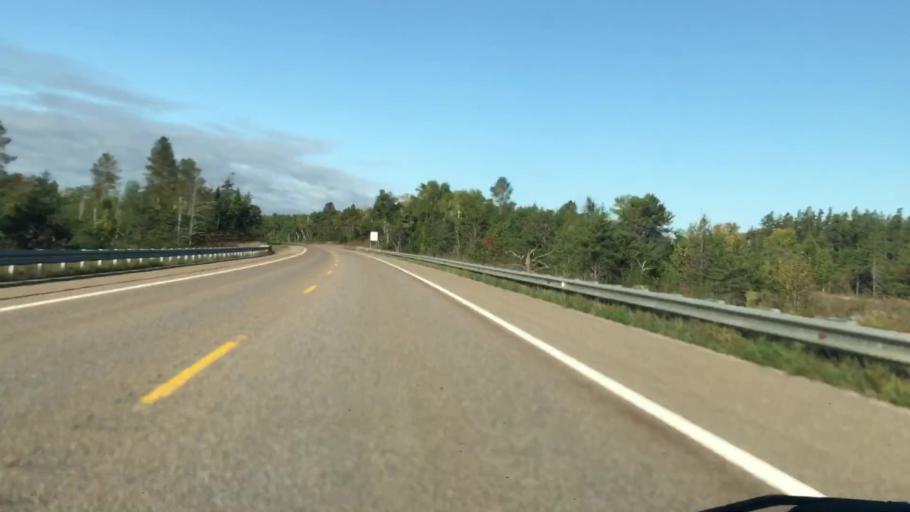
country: US
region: Michigan
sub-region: Mackinac County
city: Saint Ignace
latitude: 46.3581
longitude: -84.8867
